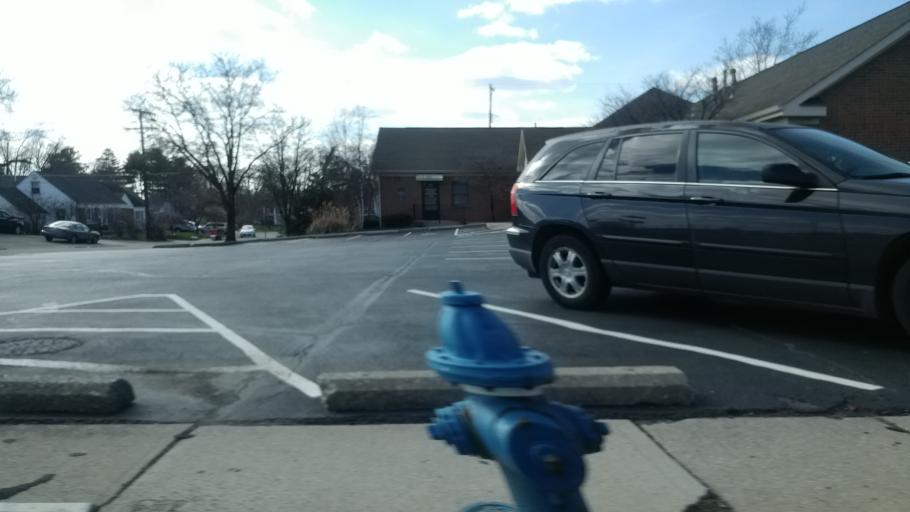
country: US
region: Ohio
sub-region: Franklin County
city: Worthington
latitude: 40.0765
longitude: -83.0188
